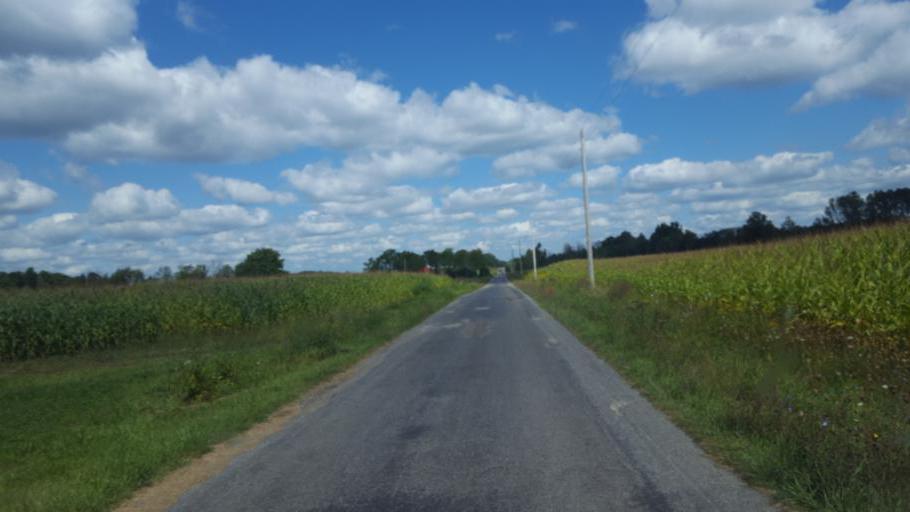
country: US
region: Ohio
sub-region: Wayne County
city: West Salem
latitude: 41.0052
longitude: -82.2025
